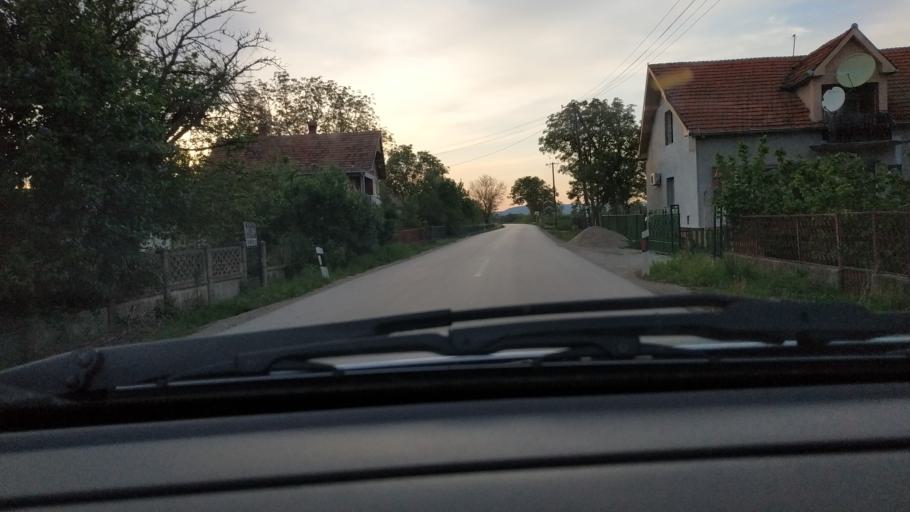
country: RS
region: Central Serbia
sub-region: Nisavski Okrug
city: Aleksinac
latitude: 43.5455
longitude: 21.6247
